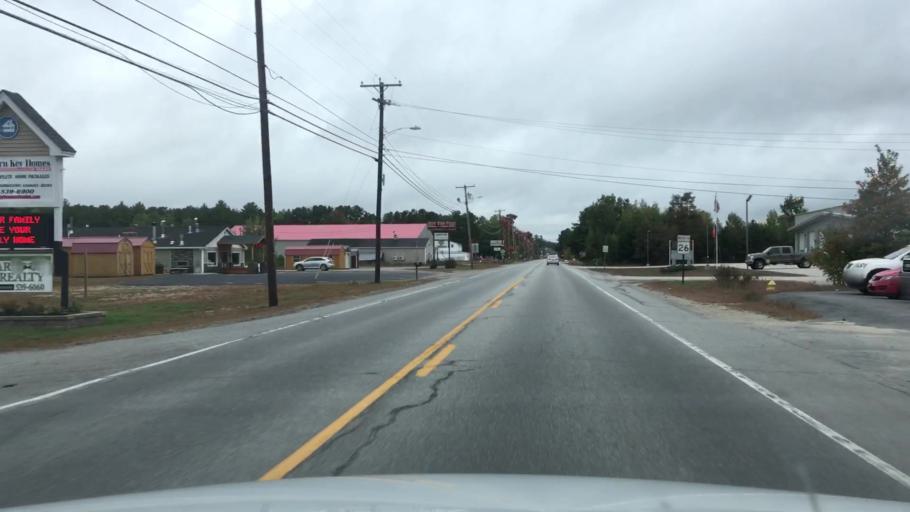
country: US
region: Maine
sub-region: Oxford County
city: Oxford
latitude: 44.1449
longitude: -70.4783
